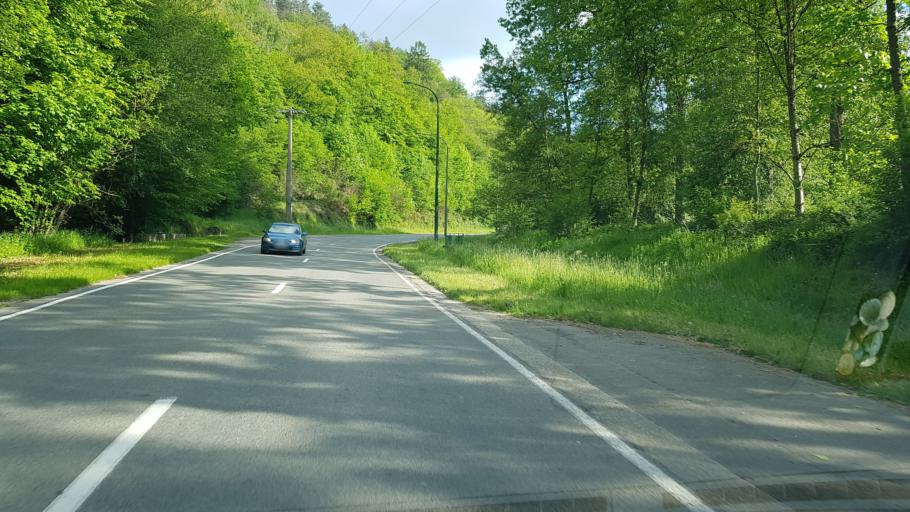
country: BE
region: Wallonia
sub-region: Province de Liege
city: Trooz
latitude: 50.5427
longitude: 5.6927
